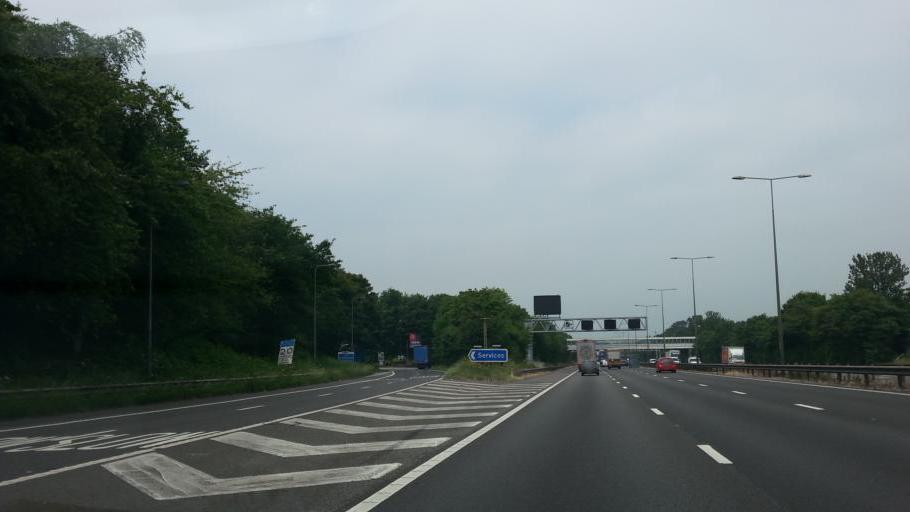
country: GB
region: England
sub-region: Staffordshire
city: Essington
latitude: 52.6410
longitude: -2.0553
